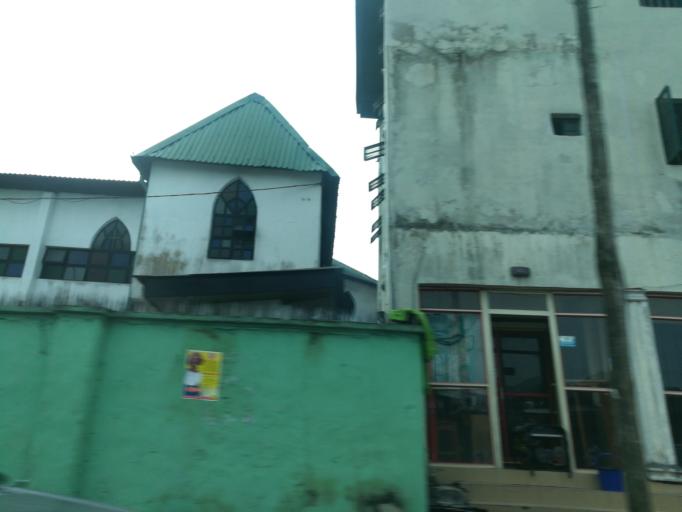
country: NG
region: Rivers
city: Port Harcourt
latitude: 4.8144
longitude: 7.0225
